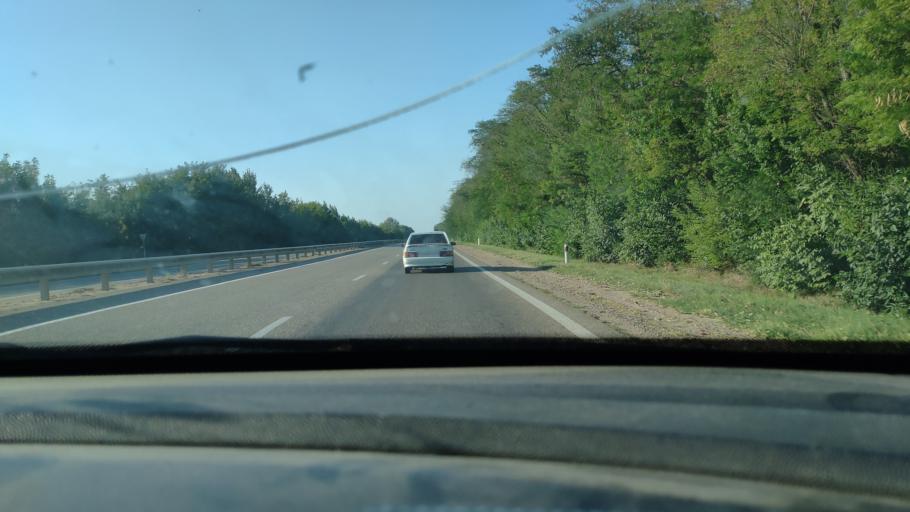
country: RU
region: Krasnodarskiy
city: Timashevsk
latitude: 45.5315
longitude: 38.9398
